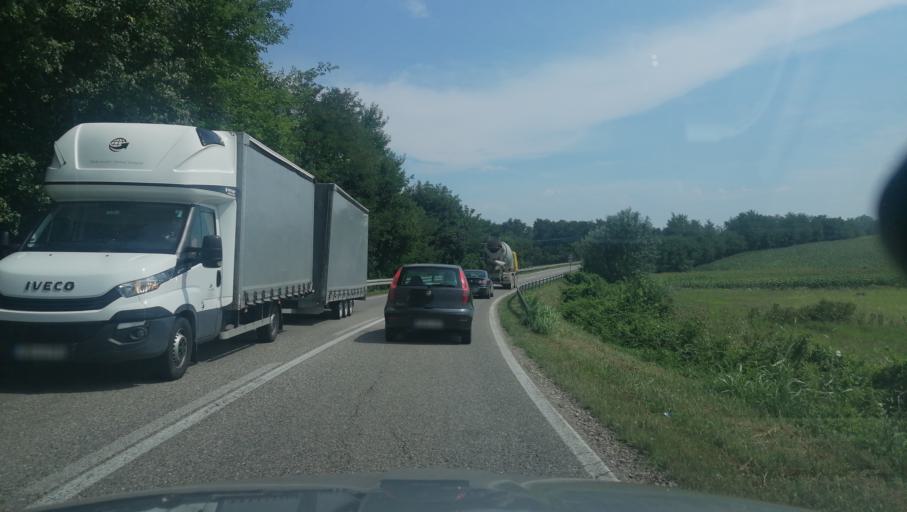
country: BA
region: Republika Srpska
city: Velika Obarska
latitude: 44.8033
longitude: 19.0793
